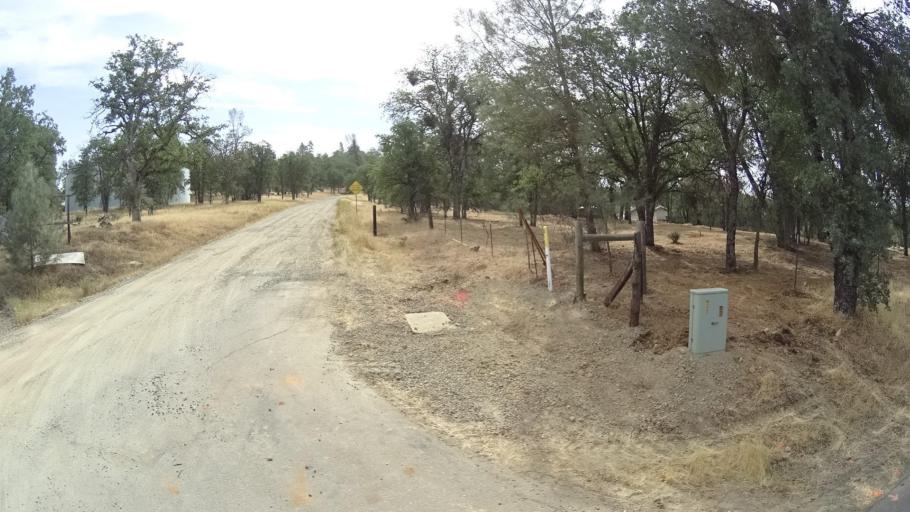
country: US
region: California
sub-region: Mariposa County
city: Midpines
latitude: 37.5427
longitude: -119.9689
